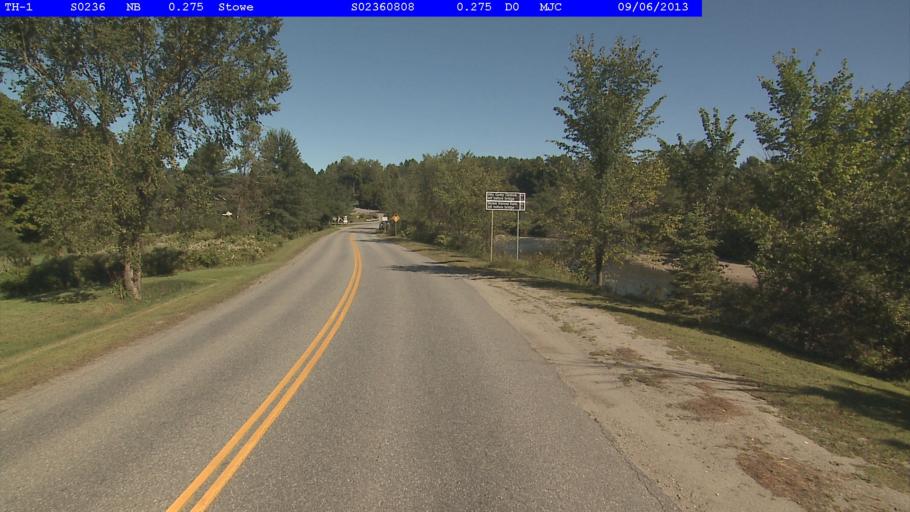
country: US
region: Vermont
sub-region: Washington County
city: Waterbury
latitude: 44.4389
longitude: -72.7139
